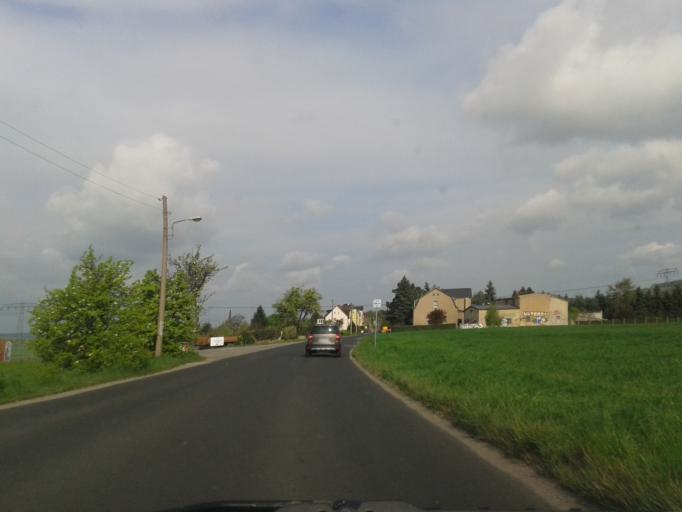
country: DE
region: Saxony
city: Radebeul
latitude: 51.0987
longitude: 13.6497
